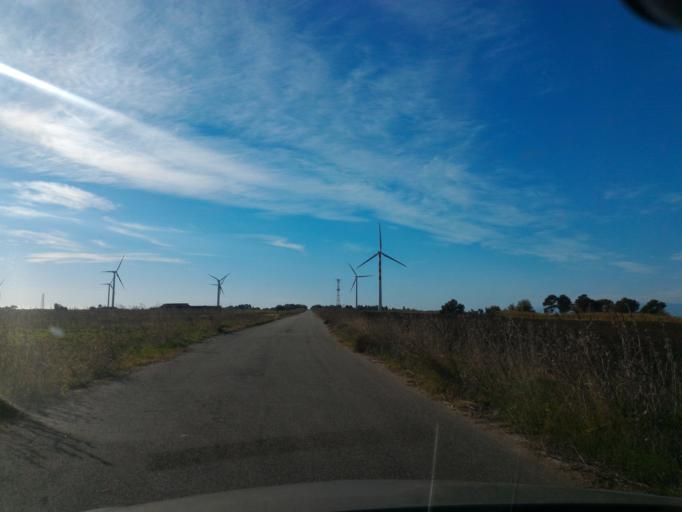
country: IT
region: Calabria
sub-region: Provincia di Crotone
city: Le Castella
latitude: 38.9564
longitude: 17.0181
